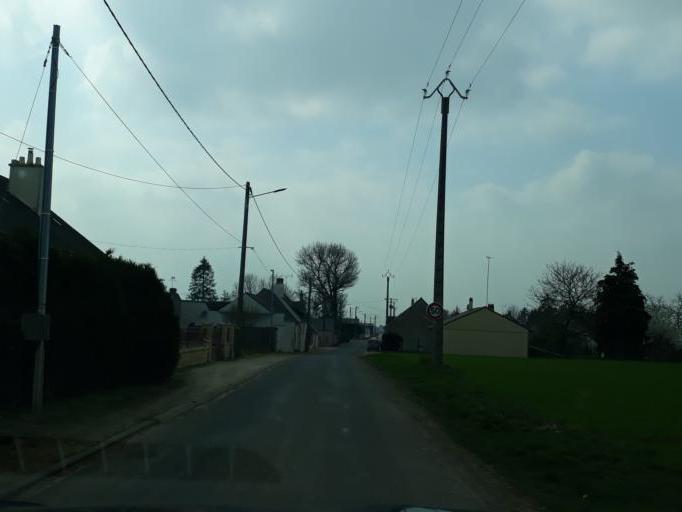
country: FR
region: Centre
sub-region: Departement d'Eure-et-Loir
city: Baigneaux
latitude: 48.0677
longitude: 1.7974
